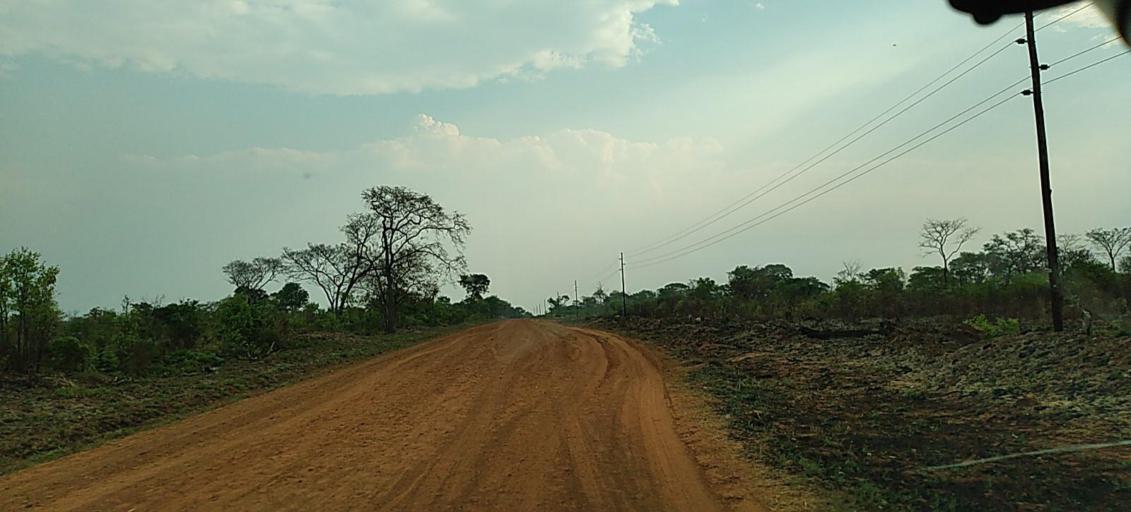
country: ZM
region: North-Western
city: Kabompo
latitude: -13.8946
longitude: 23.6582
